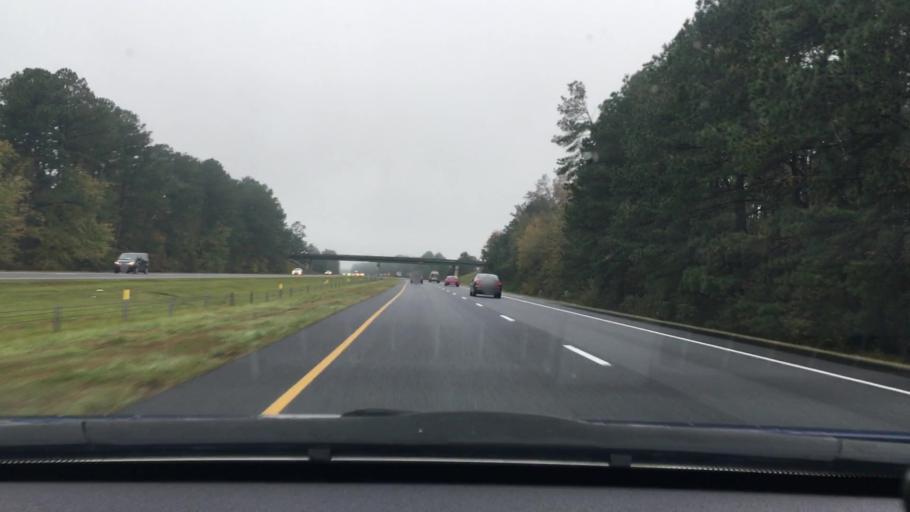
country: US
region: South Carolina
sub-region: Lee County
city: Bishopville
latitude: 34.1945
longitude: -80.1367
